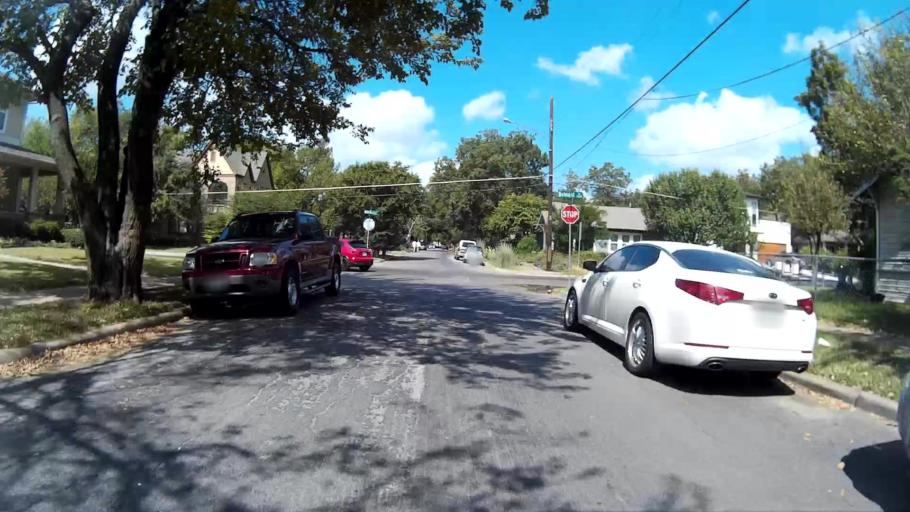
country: US
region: Texas
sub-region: Dallas County
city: Highland Park
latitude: 32.8163
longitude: -96.7785
